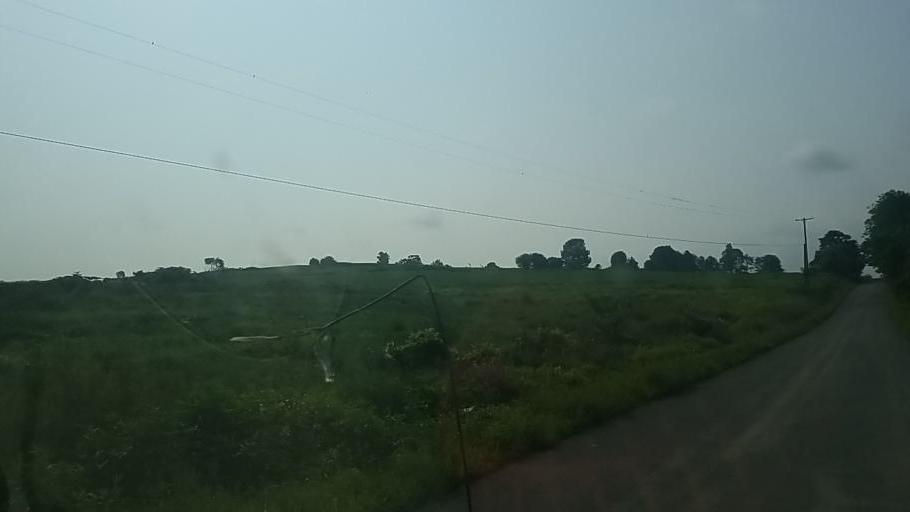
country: US
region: New York
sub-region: Montgomery County
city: Fonda
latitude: 42.9842
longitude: -74.4469
